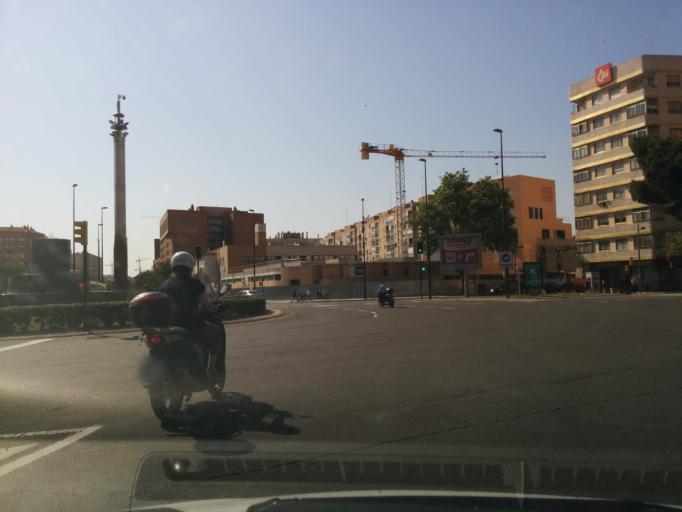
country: ES
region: Aragon
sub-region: Provincia de Zaragoza
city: Zaragoza
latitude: 41.6404
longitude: -0.8742
